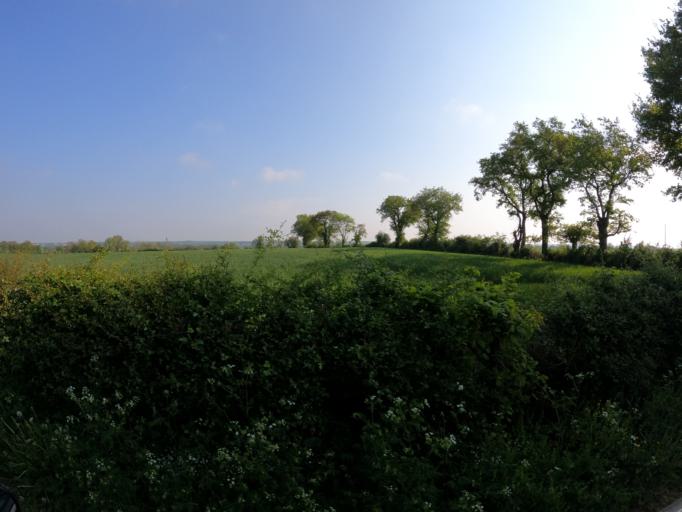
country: FR
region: Pays de la Loire
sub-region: Departement de Maine-et-Loire
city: Saint-Andre-de-la-Marche
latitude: 47.0707
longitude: -0.9835
